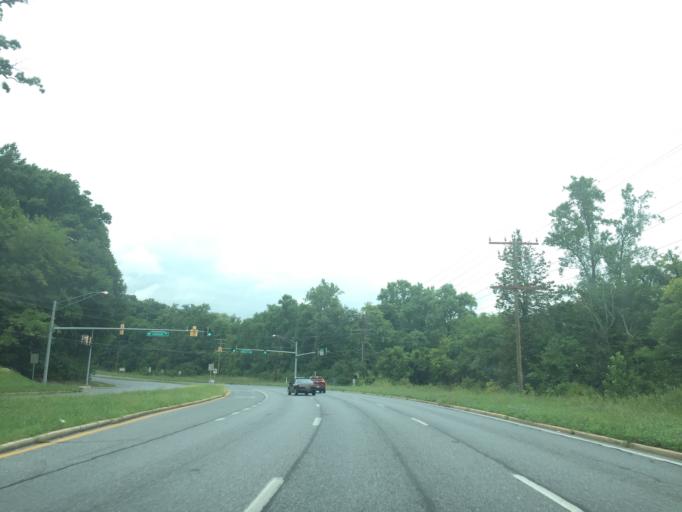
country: US
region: Maryland
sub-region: Baltimore County
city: Woodlawn
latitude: 39.3104
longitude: -76.7161
